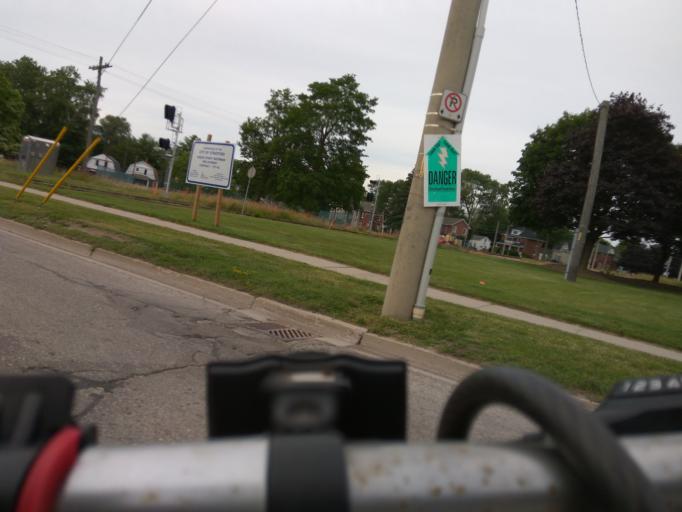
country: CA
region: Ontario
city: Stratford
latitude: 43.3639
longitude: -80.9785
